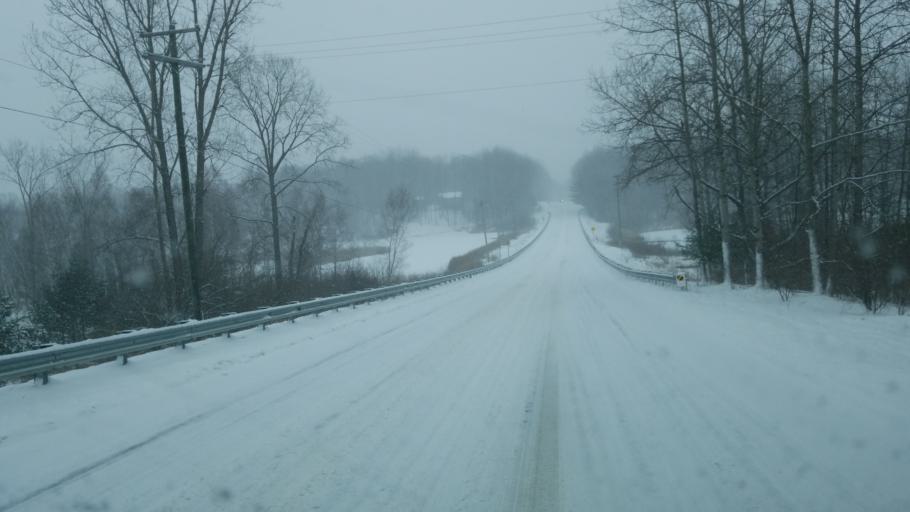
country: US
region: Michigan
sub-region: Mecosta County
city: Canadian Lakes
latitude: 43.5907
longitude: -85.3193
